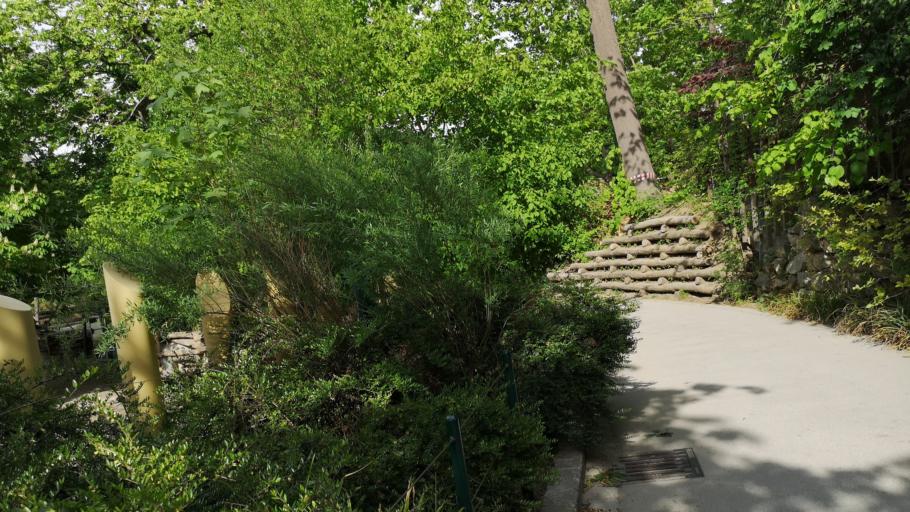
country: AT
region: Lower Austria
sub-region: Politischer Bezirk Modling
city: Vosendorf
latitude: 48.1814
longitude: 16.3083
